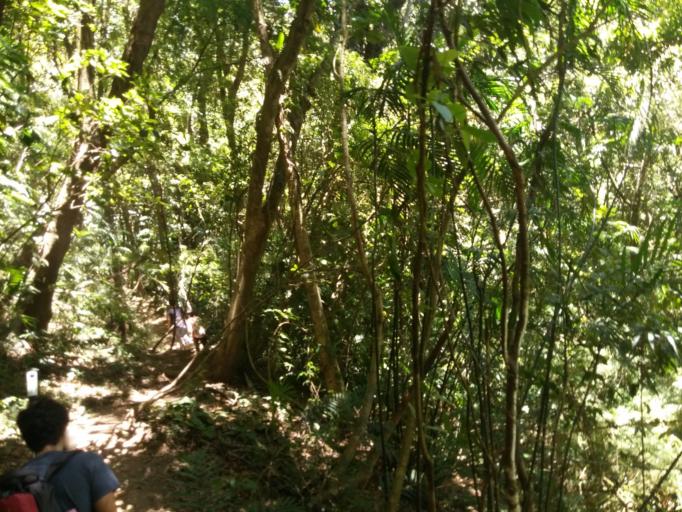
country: CR
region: Alajuela
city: Sabanilla
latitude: 10.1499
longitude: -84.2408
